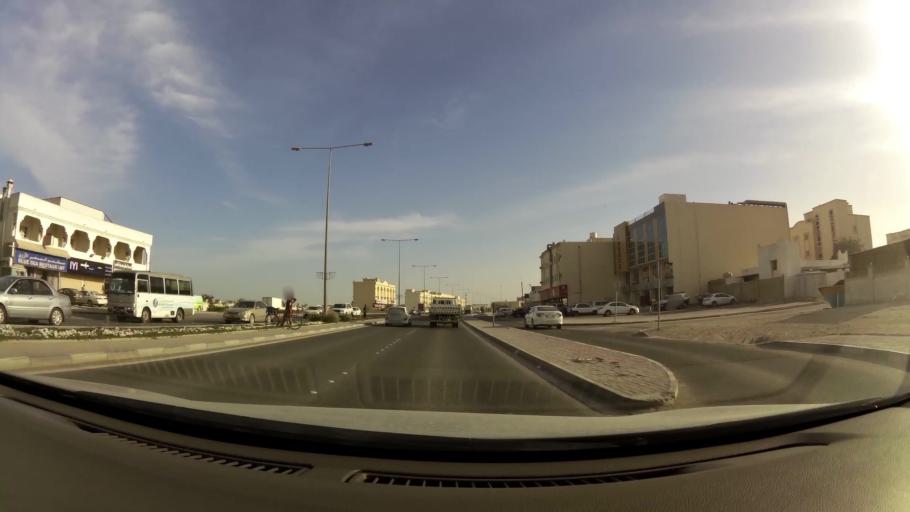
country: QA
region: Al Wakrah
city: Al Wakrah
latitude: 25.1667
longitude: 51.6077
